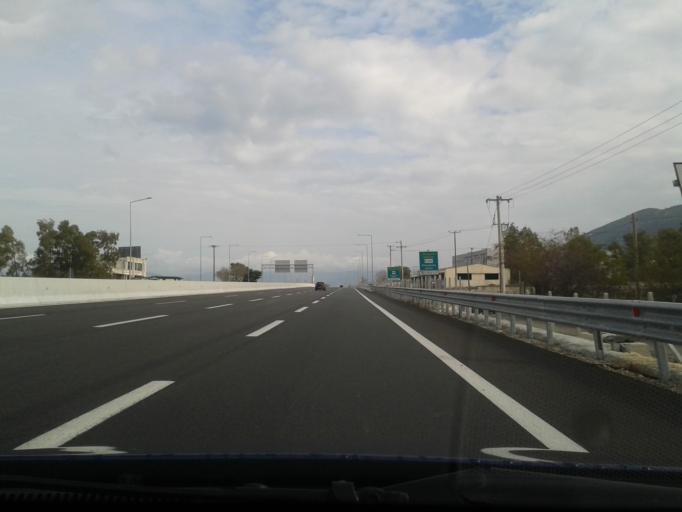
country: GR
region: West Greece
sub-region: Nomos Achaias
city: Rio
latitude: 38.3038
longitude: 21.8045
